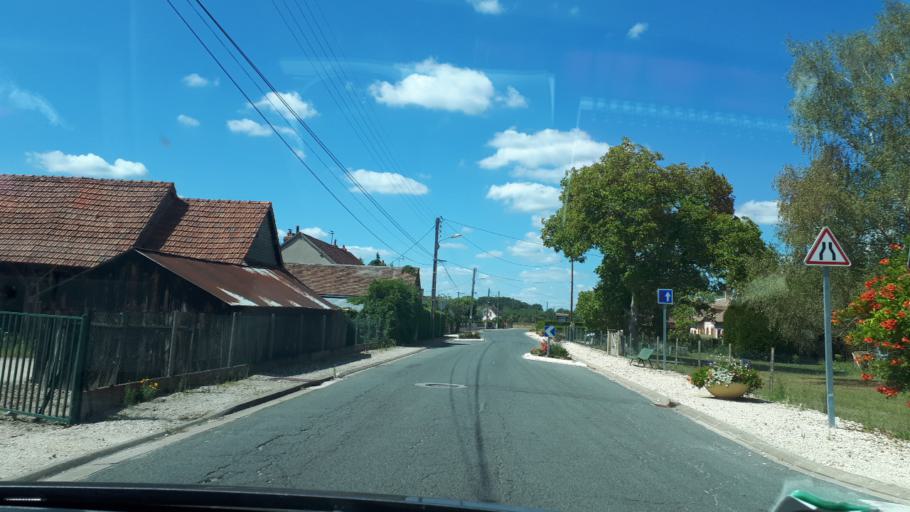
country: FR
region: Centre
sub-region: Departement du Loir-et-Cher
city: Neung-sur-Beuvron
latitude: 47.5361
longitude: 1.7972
